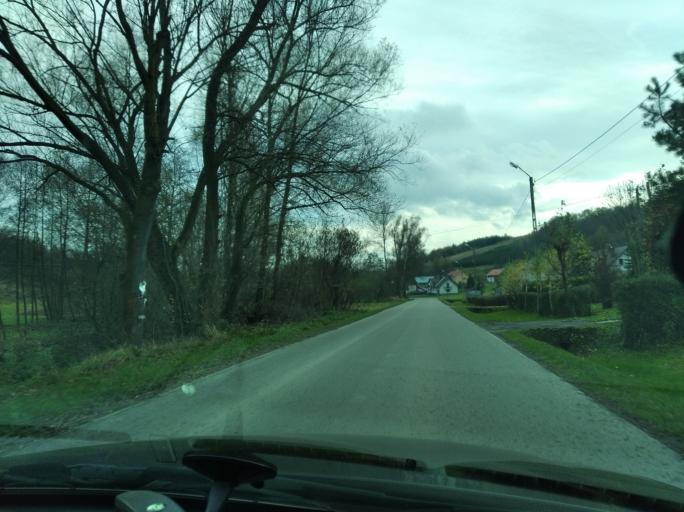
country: PL
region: Subcarpathian Voivodeship
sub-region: Powiat ropczycko-sedziszowski
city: Iwierzyce
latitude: 49.9446
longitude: 21.7511
